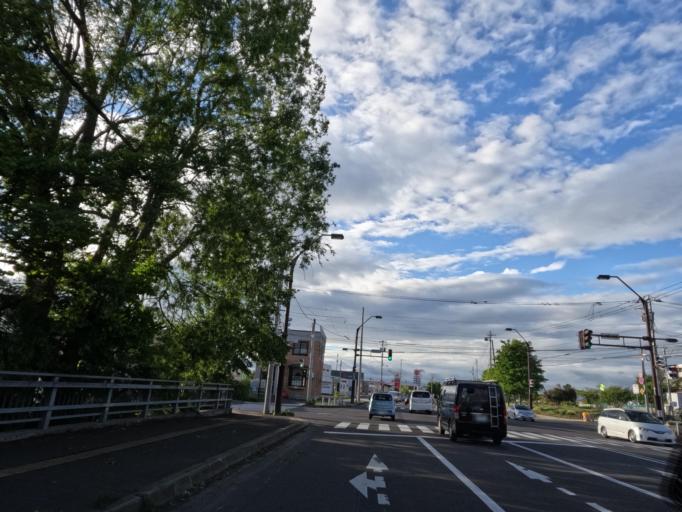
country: JP
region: Hokkaido
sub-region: Asahikawa-shi
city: Asahikawa
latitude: 43.7442
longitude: 142.3579
